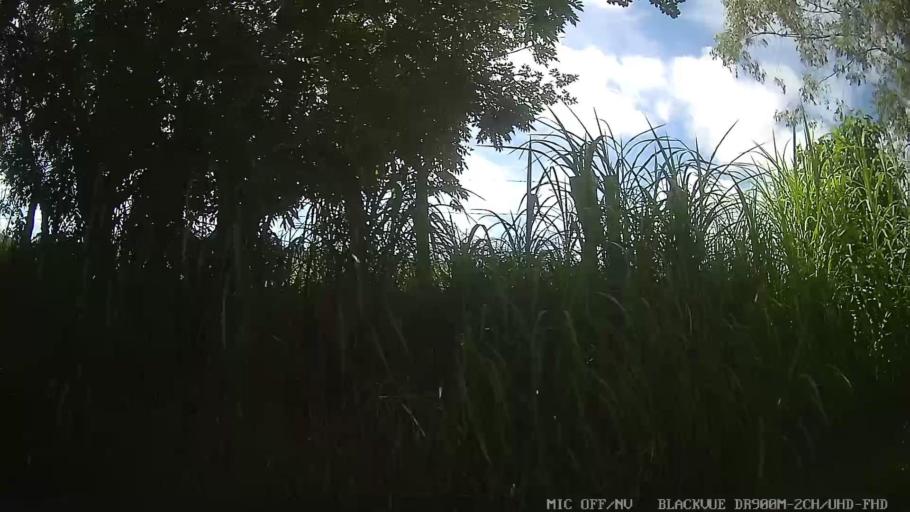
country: BR
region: Sao Paulo
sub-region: Braganca Paulista
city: Braganca Paulista
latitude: -22.9716
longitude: -46.6353
